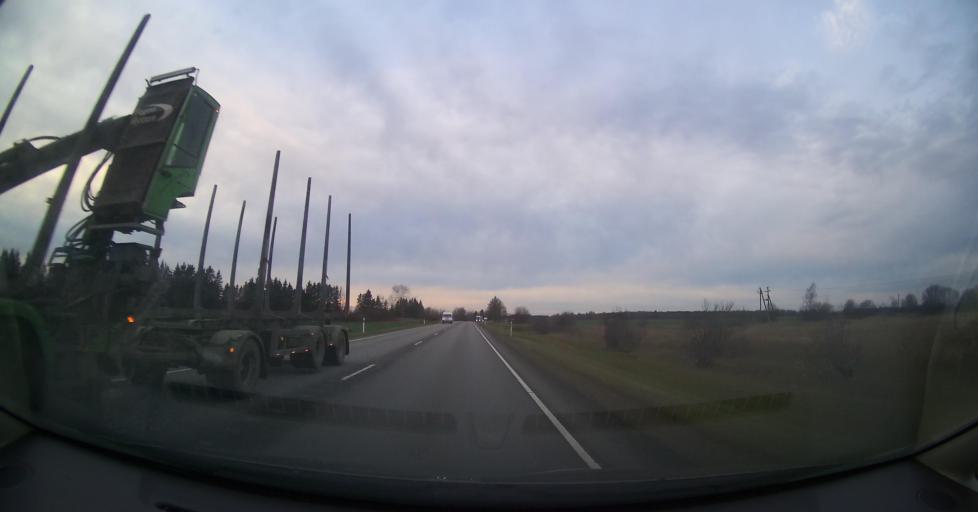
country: EE
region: Ida-Virumaa
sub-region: Kohtla-Jaerve linn
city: Kohtla-Jarve
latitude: 59.4216
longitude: 27.2057
